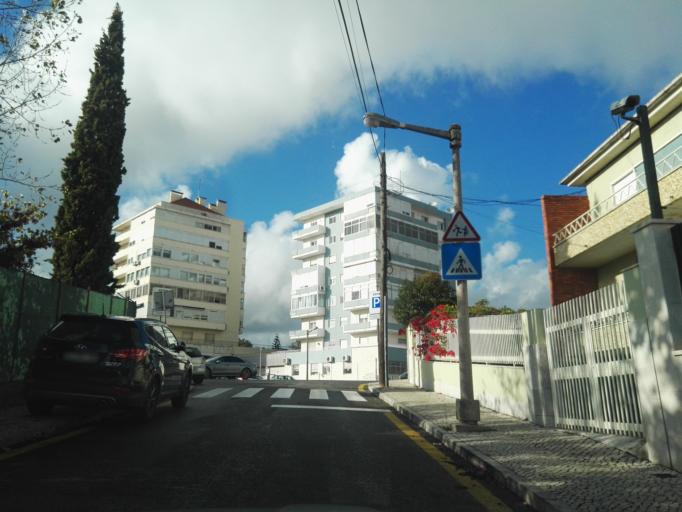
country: PT
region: Lisbon
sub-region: Lisbon
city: Lisbon
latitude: 38.7516
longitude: -9.1343
